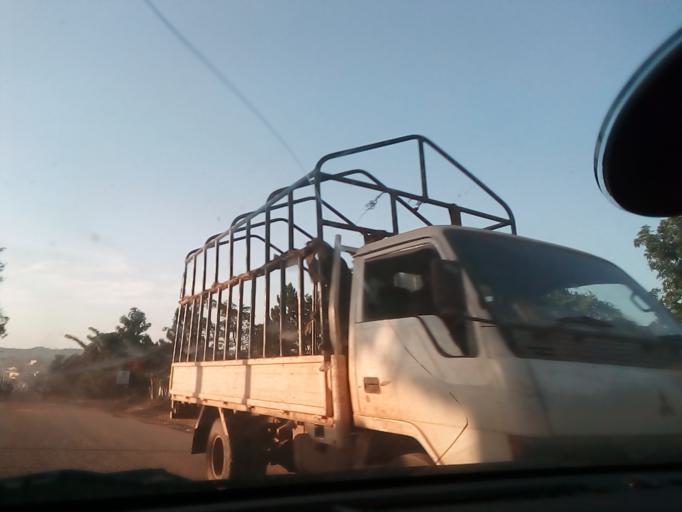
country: UG
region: Central Region
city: Masaka
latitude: -0.3276
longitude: 31.7610
